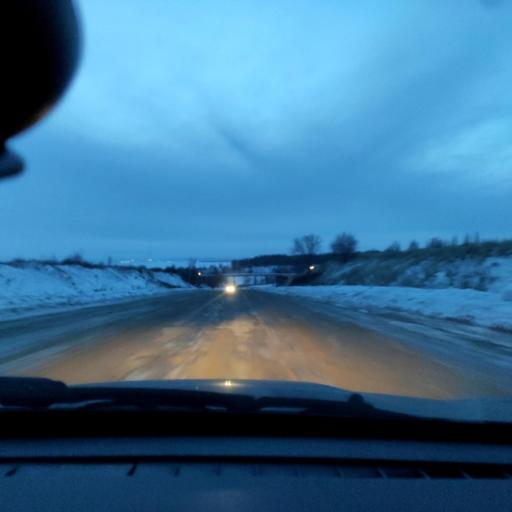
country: RU
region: Samara
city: Tol'yatti
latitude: 53.4968
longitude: 49.2753
